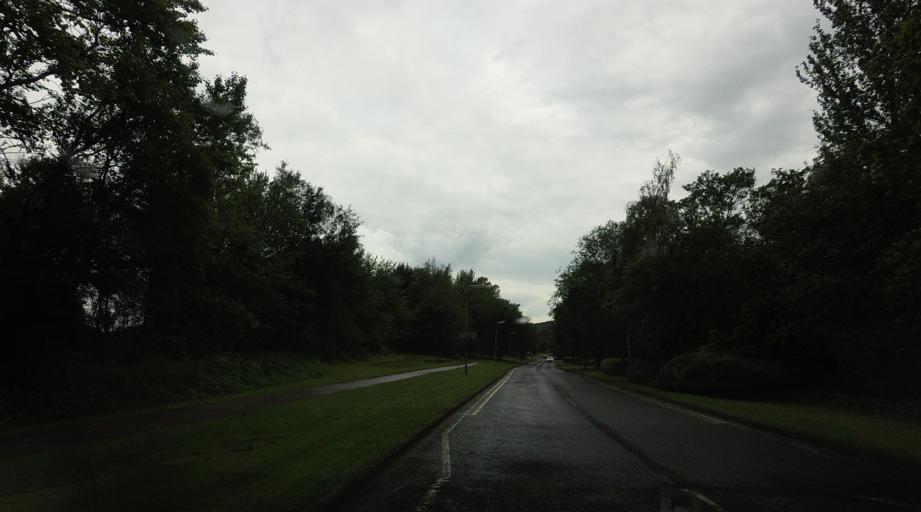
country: GB
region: Scotland
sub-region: Fife
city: Ballingry
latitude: 56.1494
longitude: -3.3318
